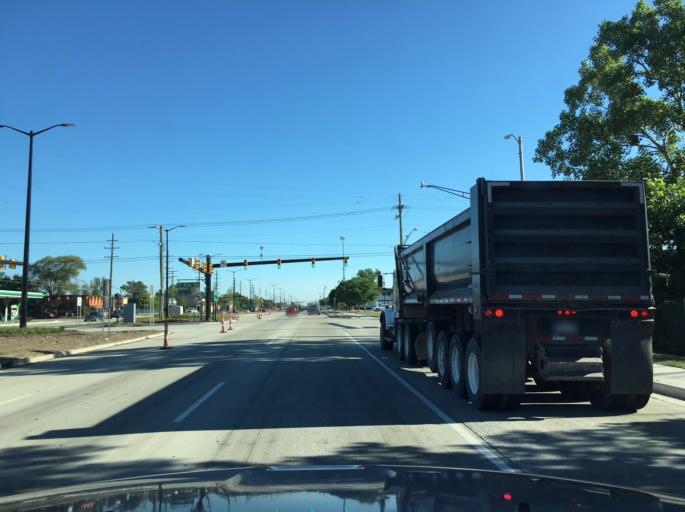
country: US
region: Michigan
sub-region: Macomb County
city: Sterling Heights
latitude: 42.5798
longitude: -83.0301
